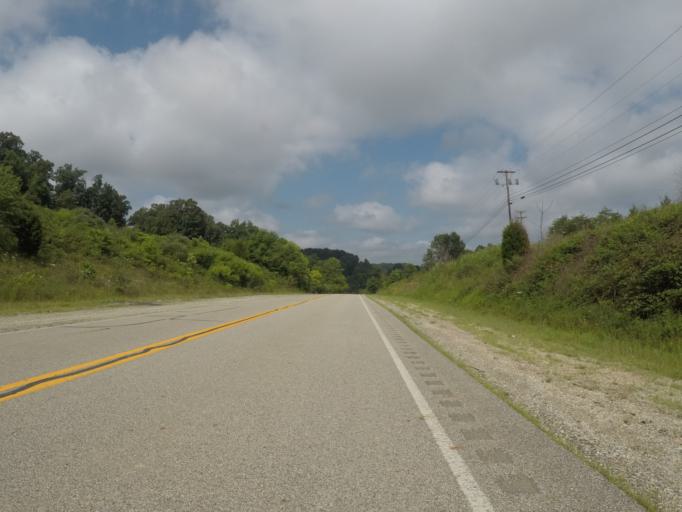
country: US
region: Kentucky
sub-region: Boyd County
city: Catlettsburg
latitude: 38.3796
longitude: -82.6151
